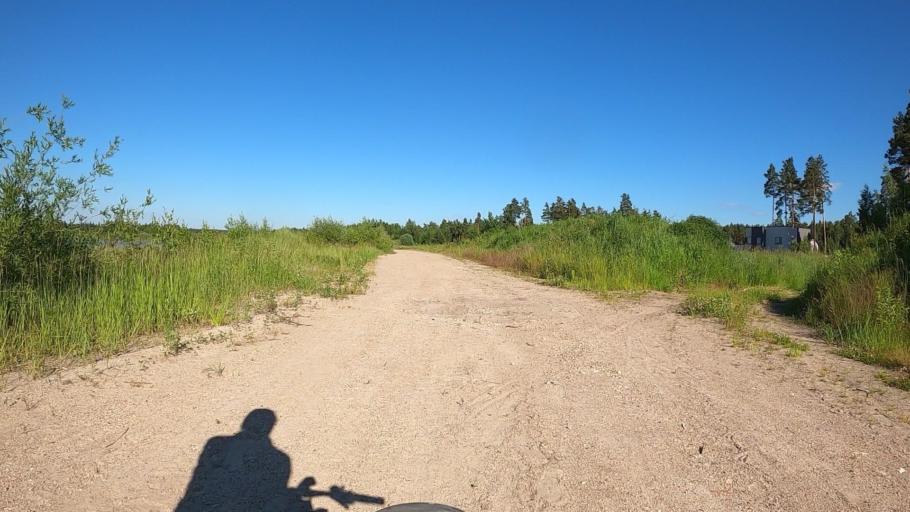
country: LV
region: Stopini
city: Ulbroka
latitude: 56.8767
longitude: 24.2794
